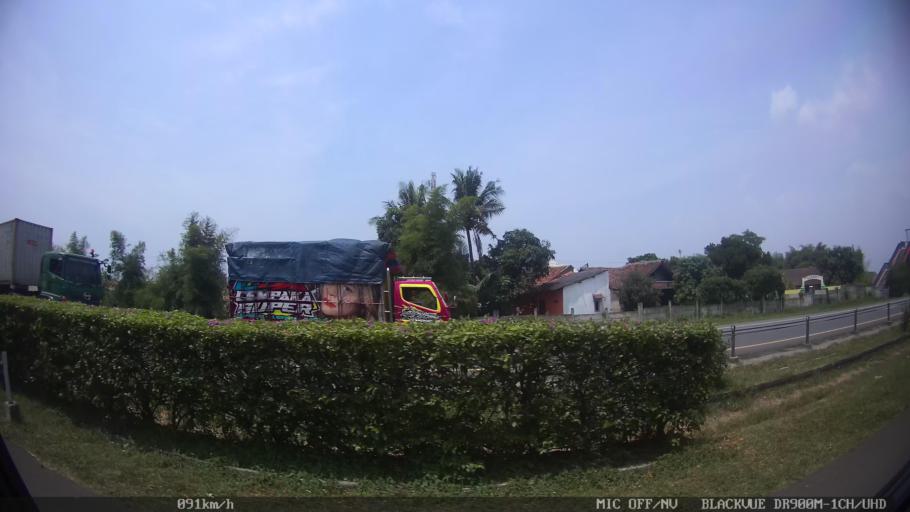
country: ID
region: Banten
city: Serang
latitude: -6.0615
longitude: 106.1231
